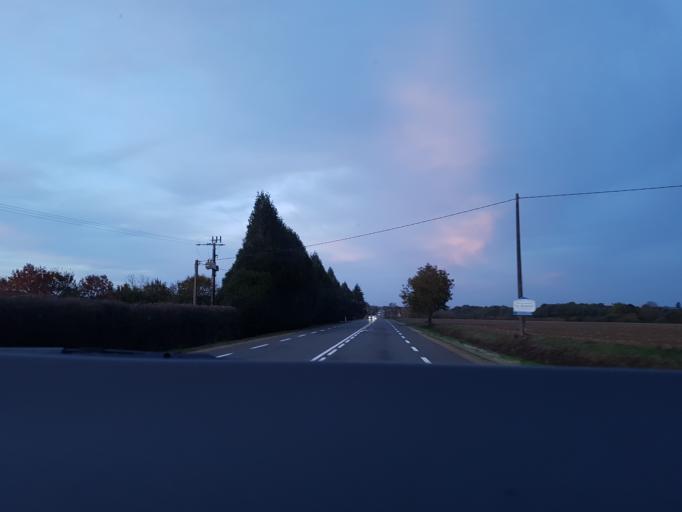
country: FR
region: Pays de la Loire
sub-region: Departement de la Mayenne
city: Ahuille
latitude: 47.9794
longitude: -0.8659
